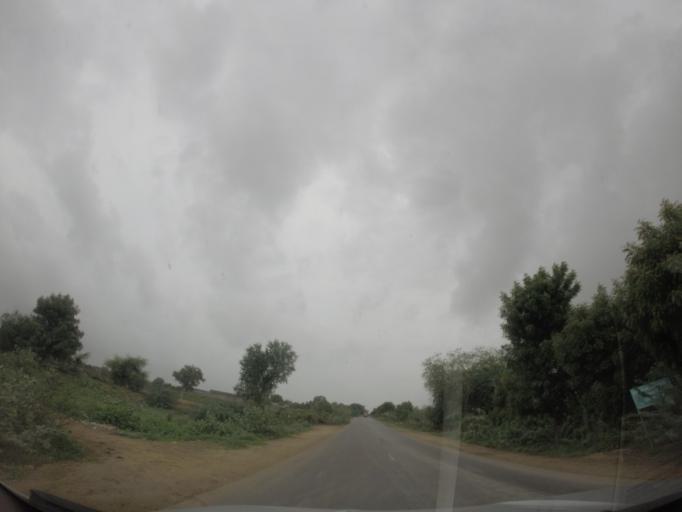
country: IN
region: Rajasthan
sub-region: Jalore
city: Sanchor
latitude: 24.6656
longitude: 71.8457
